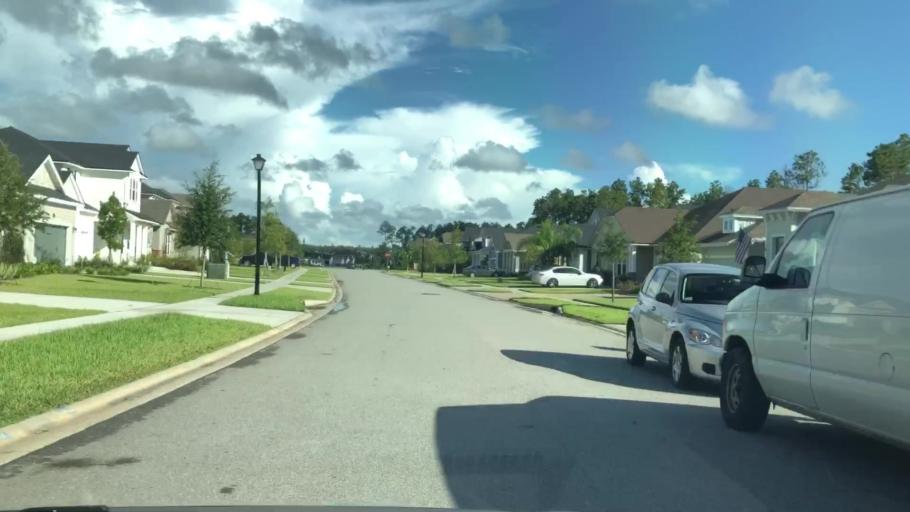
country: US
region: Florida
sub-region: Saint Johns County
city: Palm Valley
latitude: 30.1328
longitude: -81.4091
